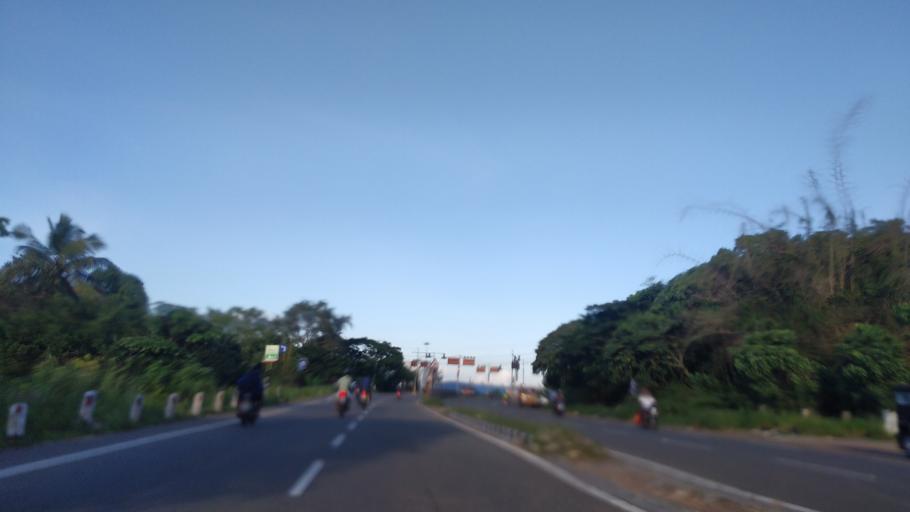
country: IN
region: Kerala
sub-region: Ernakulam
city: Elur
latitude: 10.0702
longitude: 76.3159
